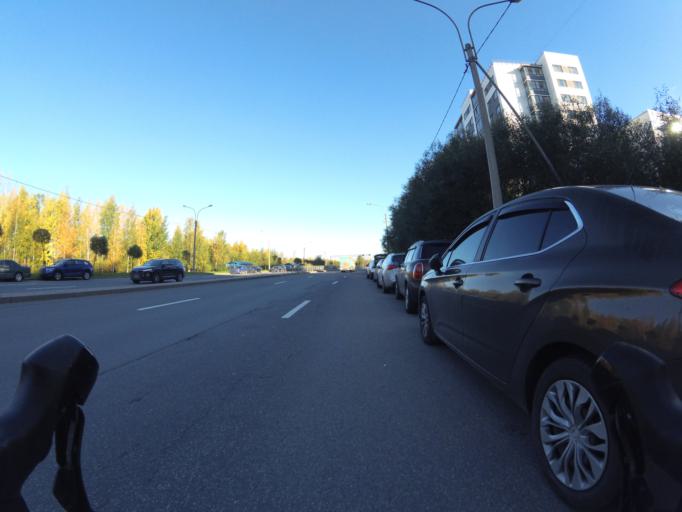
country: RU
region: Leningrad
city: Untolovo
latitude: 60.0059
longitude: 30.1978
